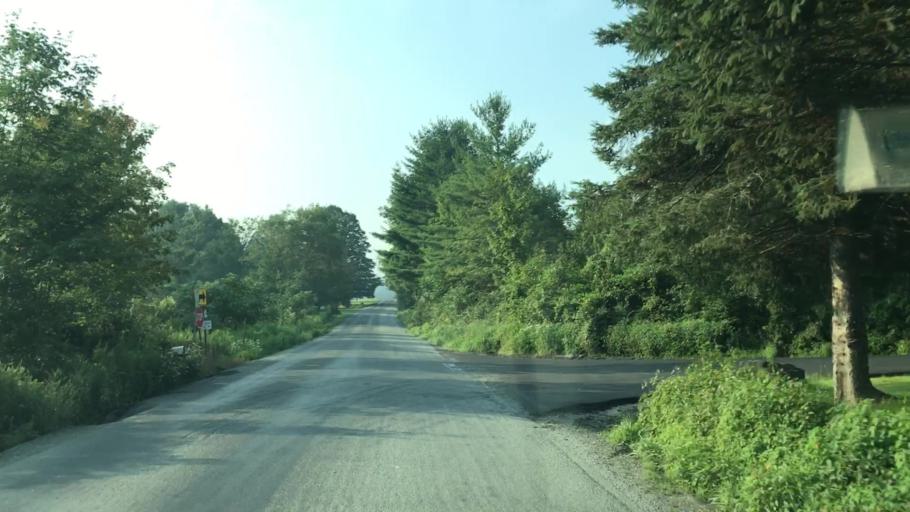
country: US
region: Pennsylvania
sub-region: Wyoming County
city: Factoryville
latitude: 41.6535
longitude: -75.7983
